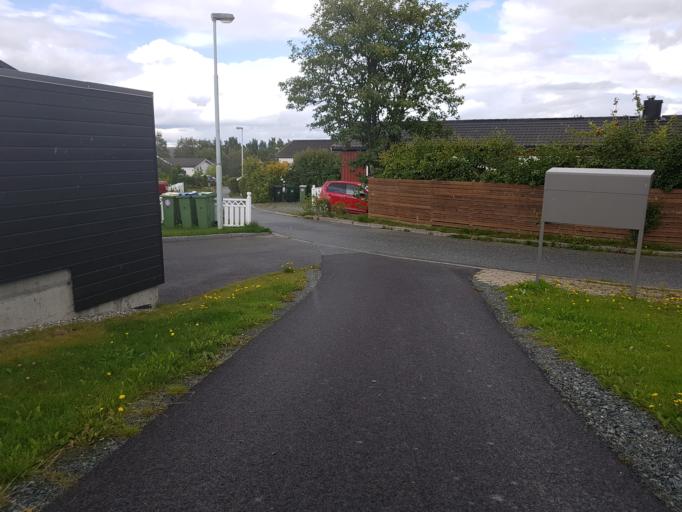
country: NO
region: Sor-Trondelag
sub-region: Trondheim
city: Trondheim
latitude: 63.4150
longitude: 10.4613
